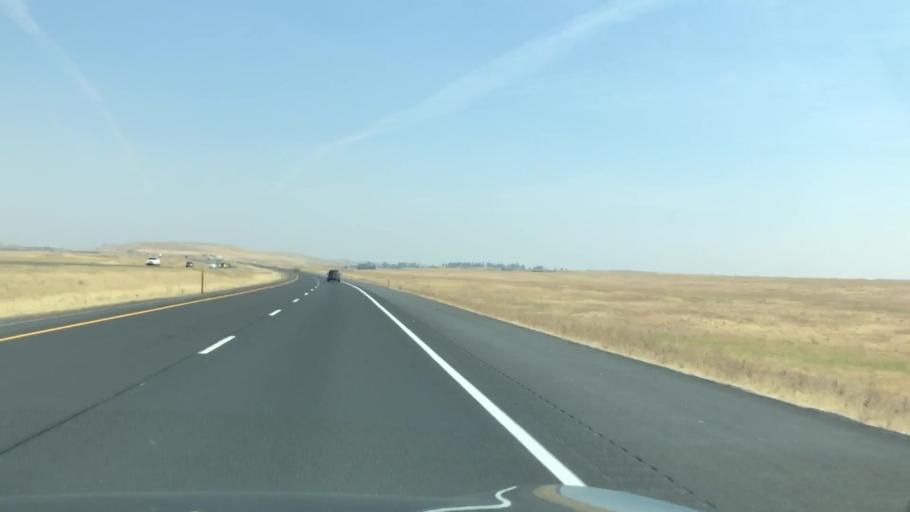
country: US
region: Washington
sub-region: Spokane County
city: Medical Lake
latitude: 47.3330
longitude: -117.9162
